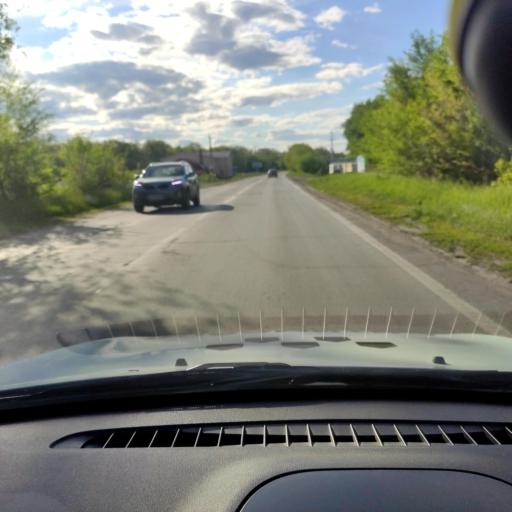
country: RU
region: Samara
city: Podstepki
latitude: 53.5833
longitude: 49.0586
